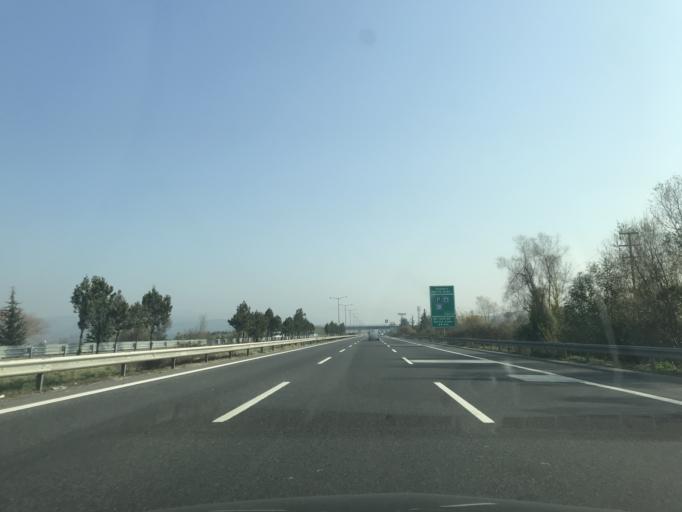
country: TR
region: Duzce
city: Duzce
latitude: 40.7906
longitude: 31.2293
